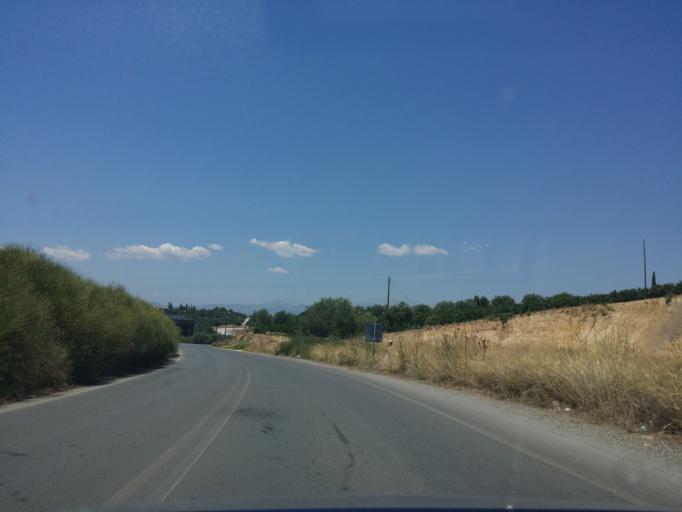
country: GR
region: Peloponnese
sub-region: Nomos Lakonias
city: Vlakhiotis
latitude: 36.8597
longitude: 22.7236
